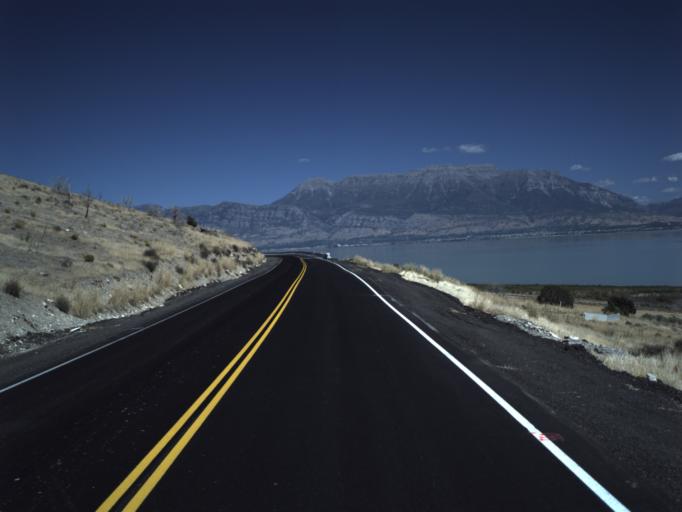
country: US
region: Utah
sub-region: Utah County
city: Saratoga Springs
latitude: 40.2275
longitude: -111.8728
